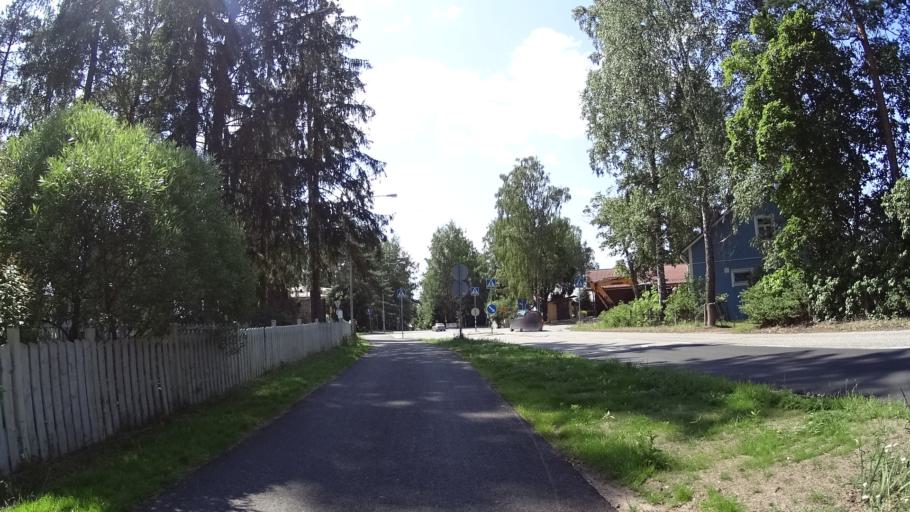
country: FI
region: Uusimaa
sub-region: Helsinki
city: Tuusula
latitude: 60.4065
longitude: 25.0128
